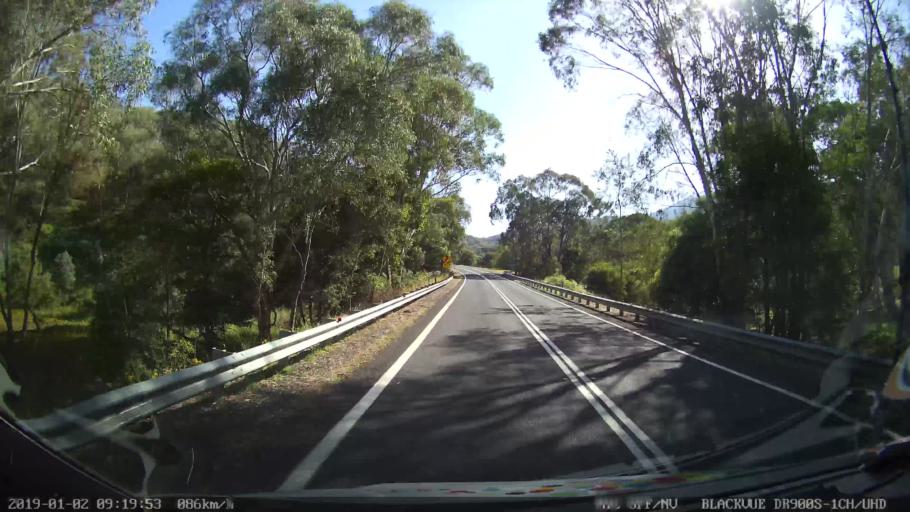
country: AU
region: New South Wales
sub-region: Tumut Shire
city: Tumut
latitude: -35.4174
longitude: 148.2784
